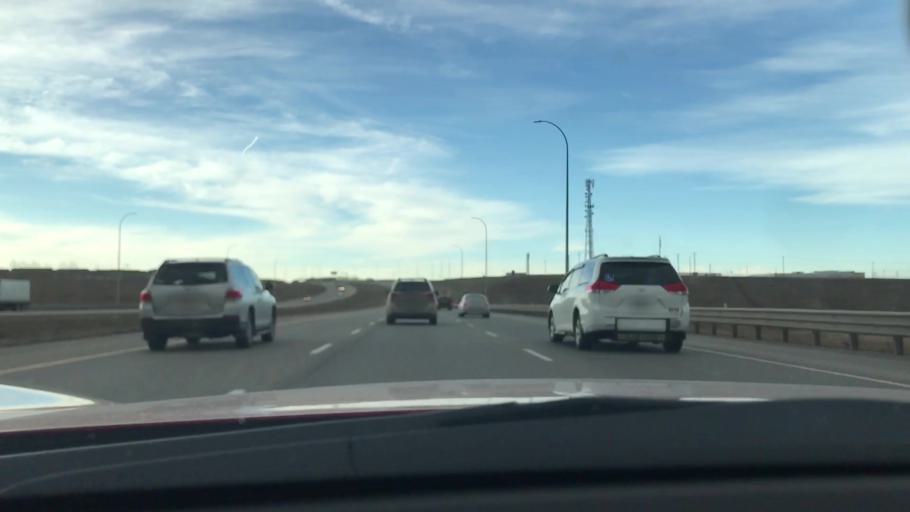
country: CA
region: Alberta
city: Calgary
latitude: 51.1514
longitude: -114.1801
